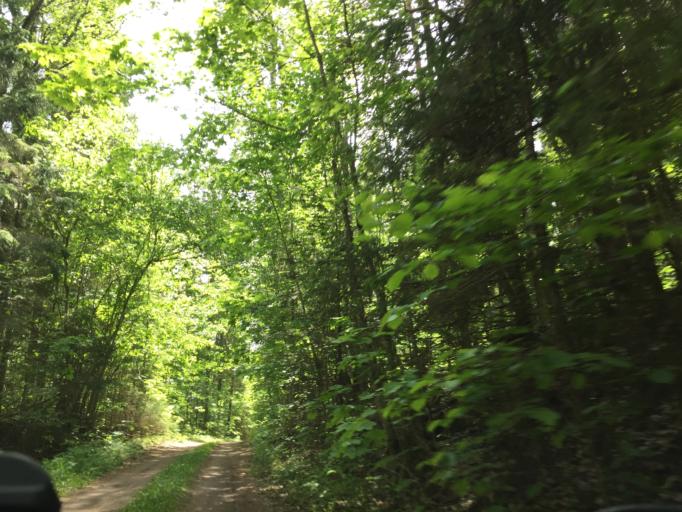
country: LV
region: Koceni
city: Koceni
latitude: 57.4410
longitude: 25.2836
